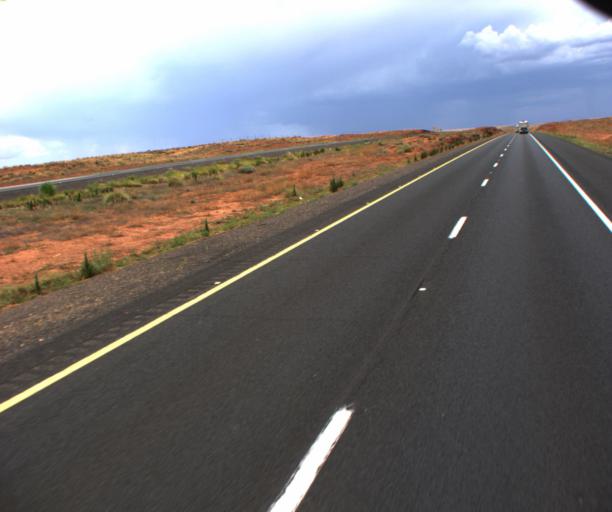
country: US
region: Arizona
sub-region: Coconino County
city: LeChee
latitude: 35.0974
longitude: -110.9510
